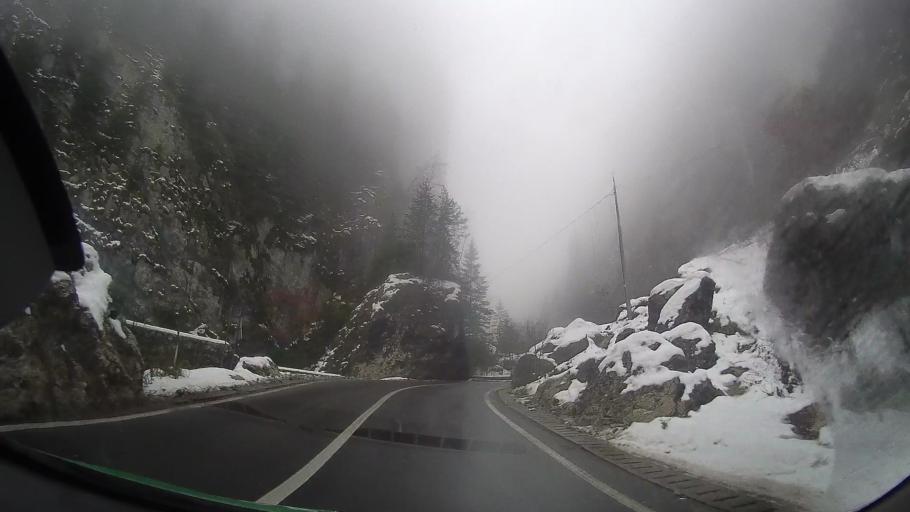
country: RO
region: Neamt
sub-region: Comuna Bicaz Chei
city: Bicaz Chei
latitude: 46.8136
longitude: 25.8281
